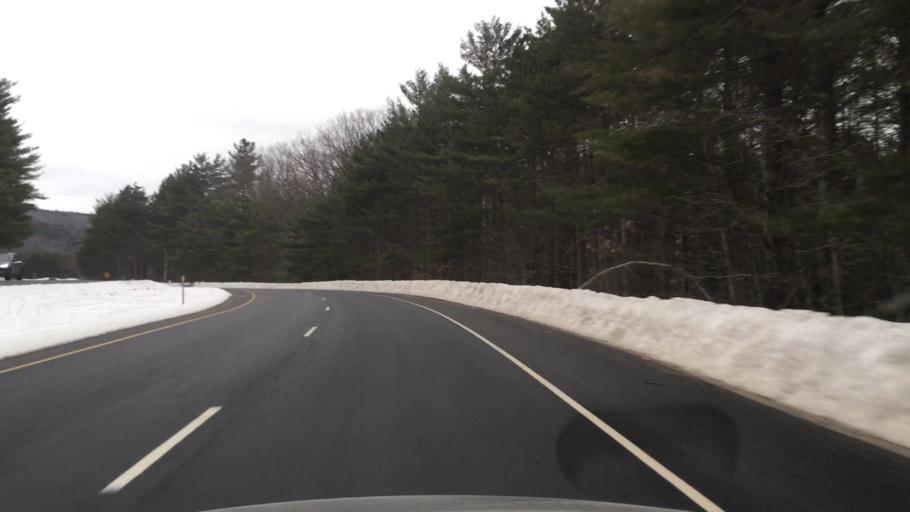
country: US
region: New Hampshire
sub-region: Merrimack County
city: Newbury
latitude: 43.3377
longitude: -72.0735
